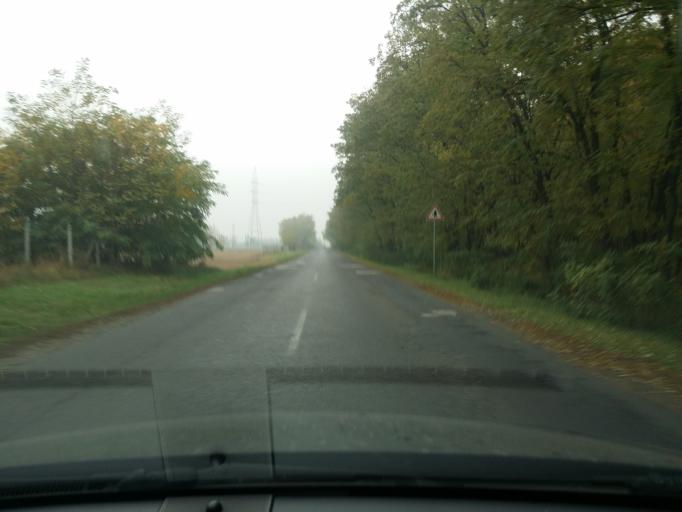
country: HU
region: Szabolcs-Szatmar-Bereg
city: Nyirbogdany
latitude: 48.0709
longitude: 21.8600
